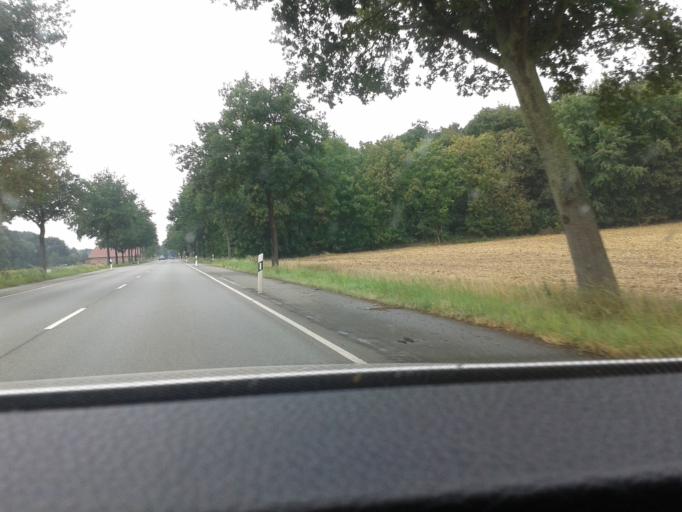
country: DE
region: Lower Saxony
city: Osloss
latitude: 52.4678
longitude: 10.6933
